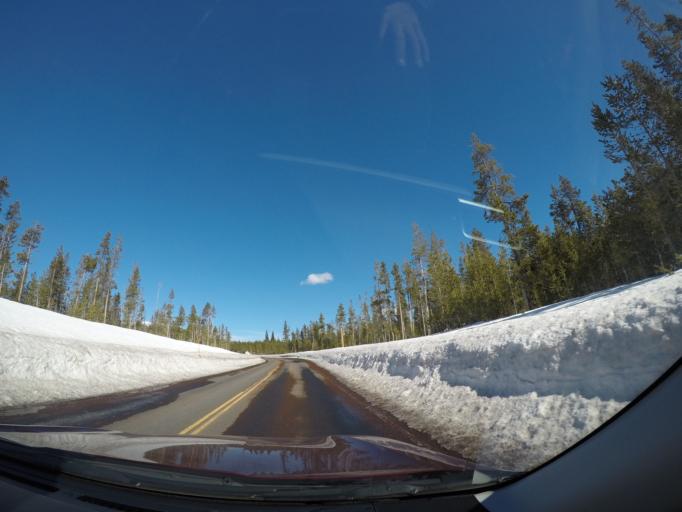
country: US
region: Oregon
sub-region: Deschutes County
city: Sunriver
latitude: 43.9613
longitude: -121.6155
